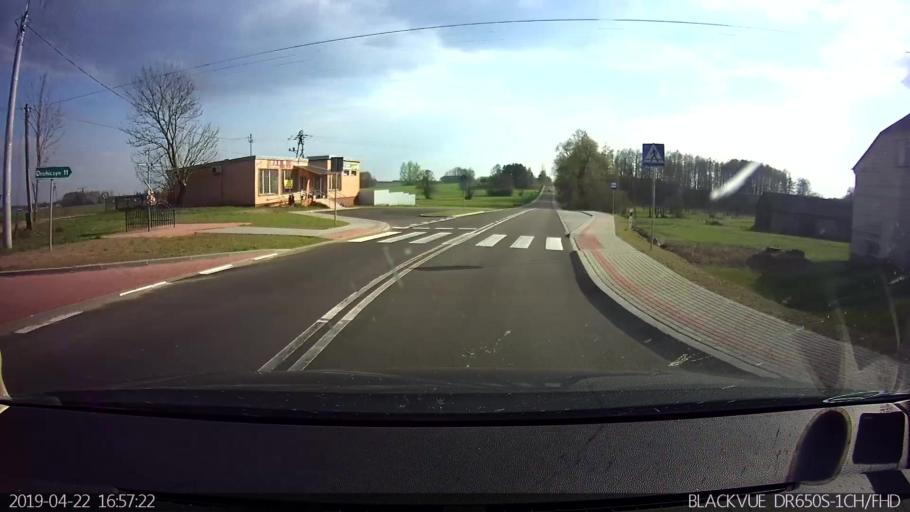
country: PL
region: Podlasie
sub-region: Powiat siemiatycki
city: Siemiatycze
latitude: 52.4809
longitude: 22.7601
